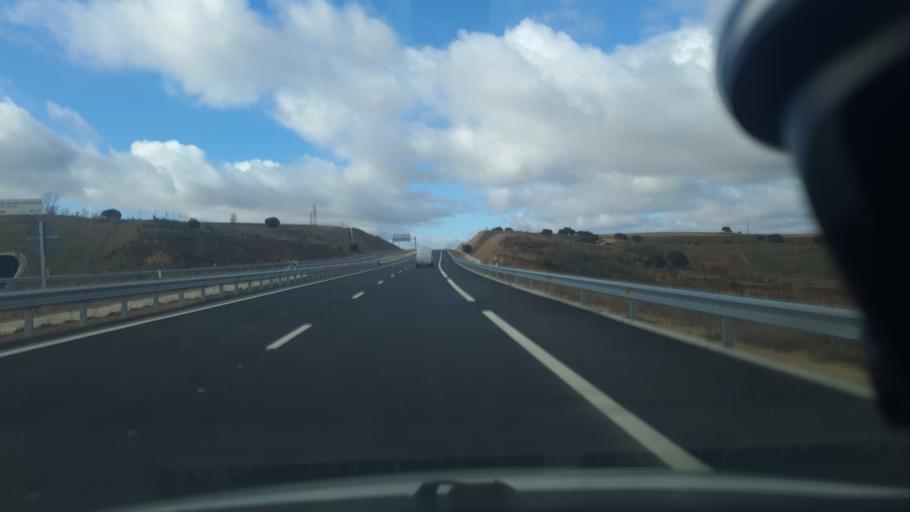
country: ES
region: Castille and Leon
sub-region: Provincia de Segovia
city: Segovia
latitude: 40.9190
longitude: -4.1246
